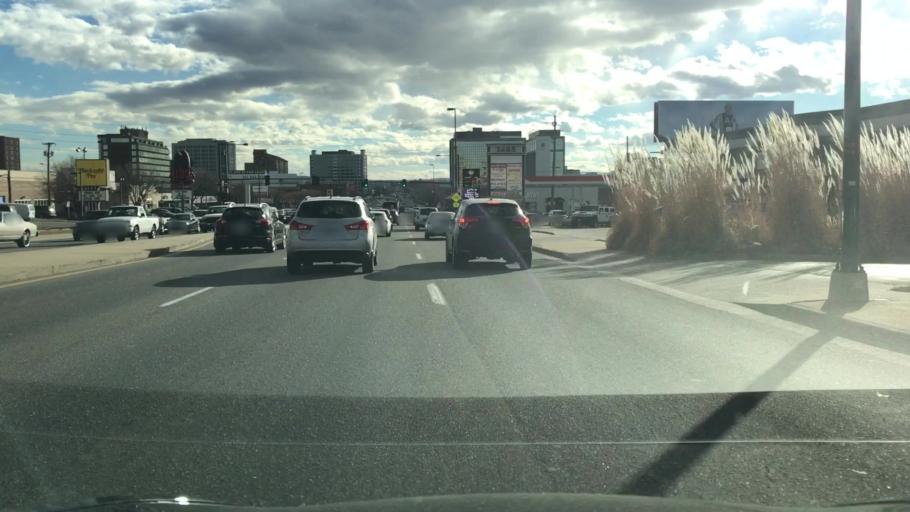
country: US
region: Colorado
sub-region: Arapahoe County
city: Glendale
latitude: 39.6906
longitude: -104.9408
